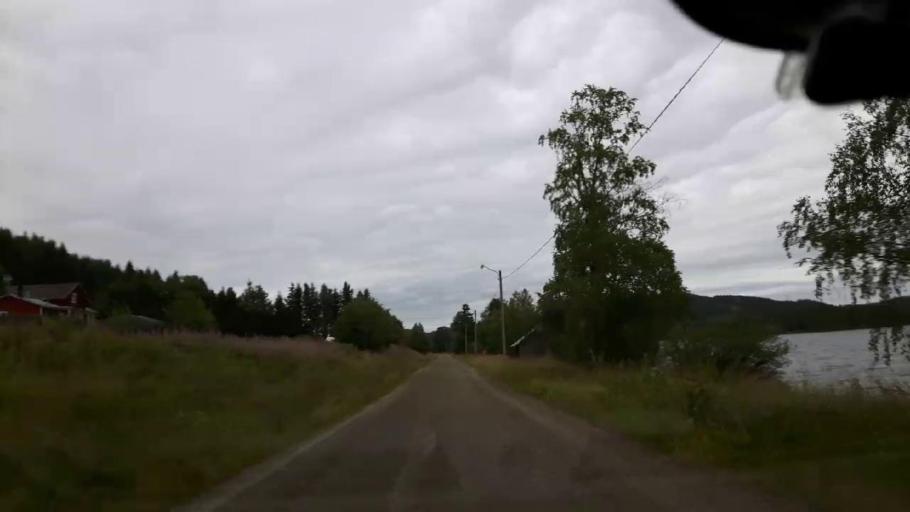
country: SE
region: Jaemtland
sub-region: Braecke Kommun
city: Braecke
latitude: 62.9965
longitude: 15.3822
